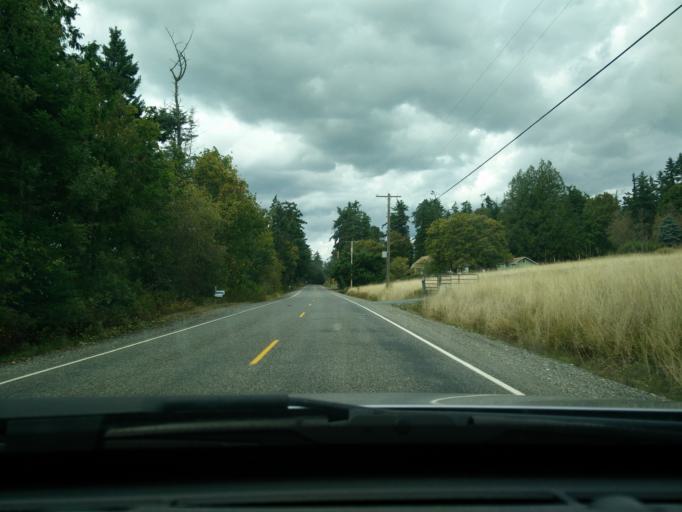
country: US
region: Washington
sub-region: Skagit County
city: Anacortes
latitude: 48.5084
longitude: -122.4822
